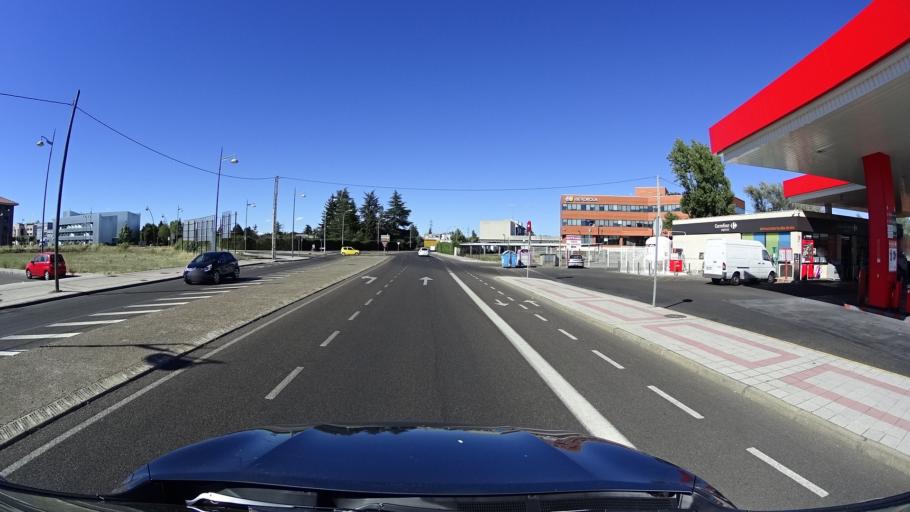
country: ES
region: Castille and Leon
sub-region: Provincia de Leon
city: Leon
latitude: 42.6082
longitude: -5.5569
